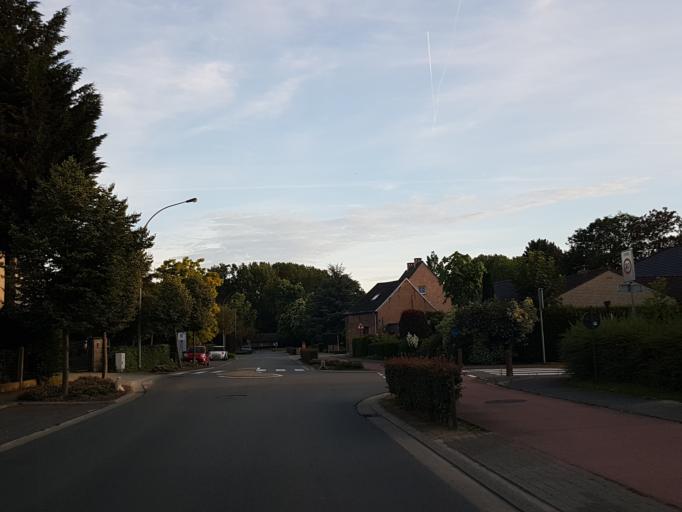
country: BE
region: Flanders
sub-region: Provincie Vlaams-Brabant
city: Londerzeel
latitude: 50.9906
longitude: 4.2659
